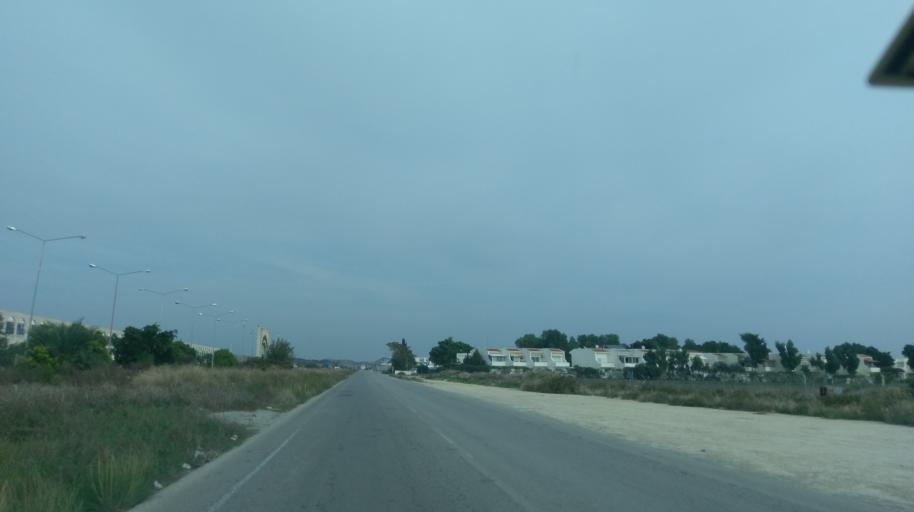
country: CY
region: Ammochostos
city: Trikomo
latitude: 35.3239
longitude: 33.9650
